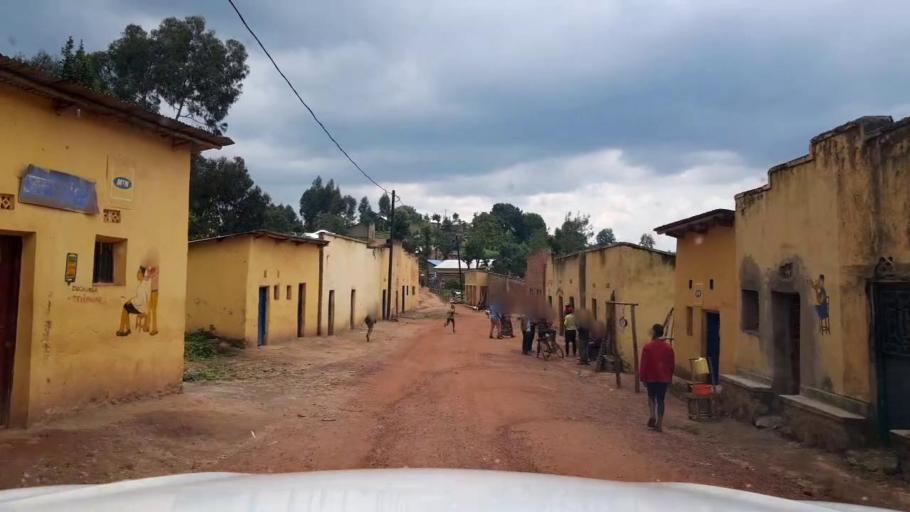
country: UG
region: Western Region
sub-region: Kabale District
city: Kabale
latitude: -1.4331
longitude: 29.8699
